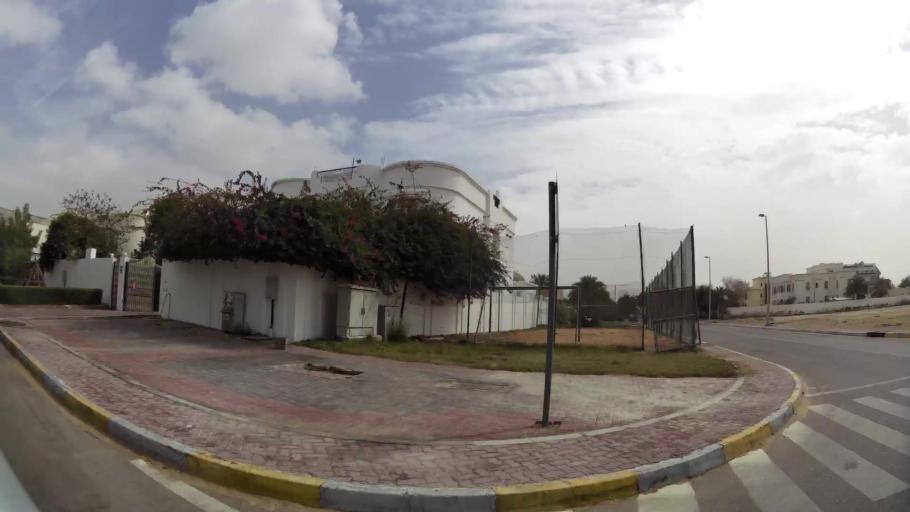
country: AE
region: Abu Dhabi
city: Abu Dhabi
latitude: 24.4046
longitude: 54.5156
